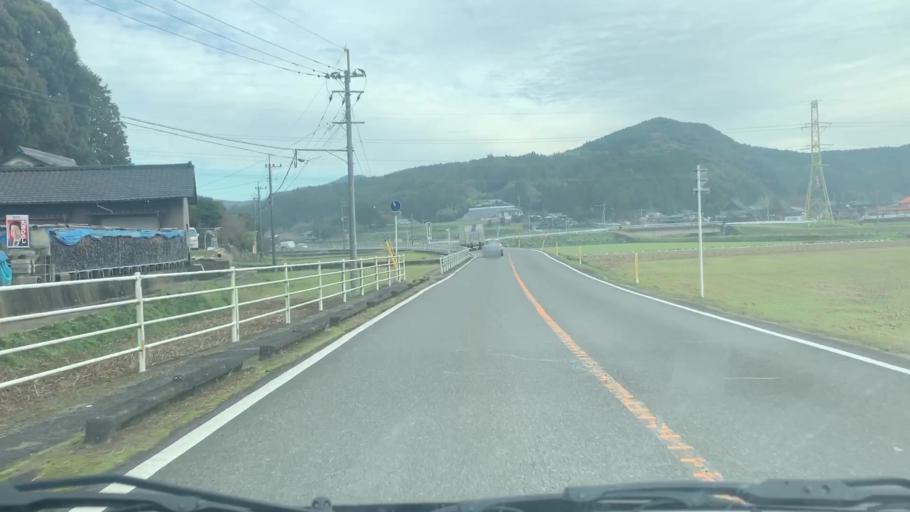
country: JP
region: Saga Prefecture
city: Takeocho-takeo
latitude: 33.2313
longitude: 129.9654
